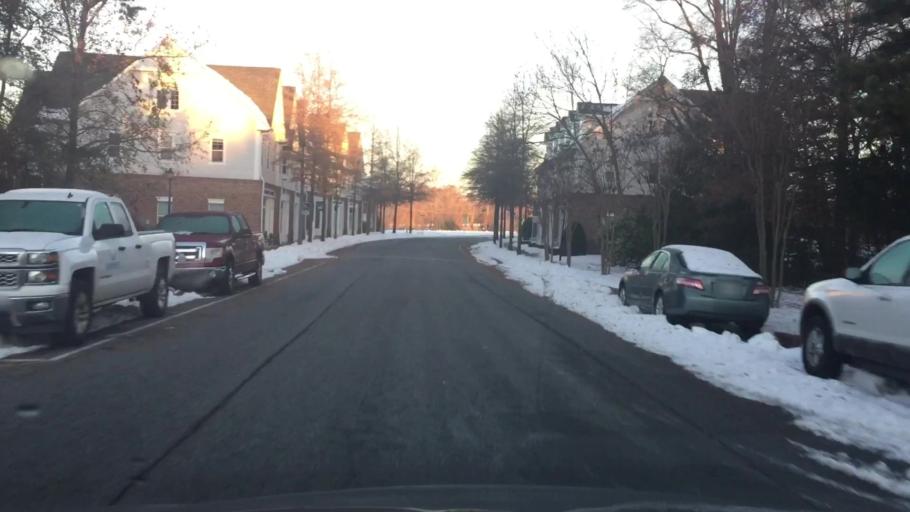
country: US
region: North Carolina
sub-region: Mecklenburg County
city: Cornelius
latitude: 35.4995
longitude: -80.8632
